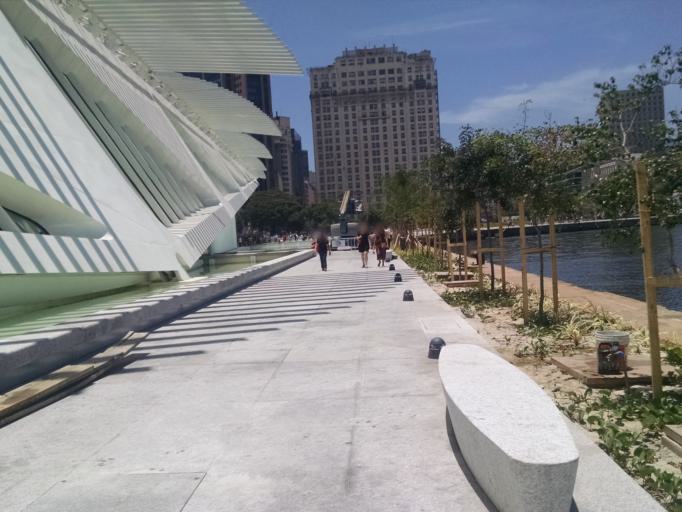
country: BR
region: Rio de Janeiro
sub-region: Rio De Janeiro
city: Rio de Janeiro
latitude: -22.8941
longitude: -43.1798
